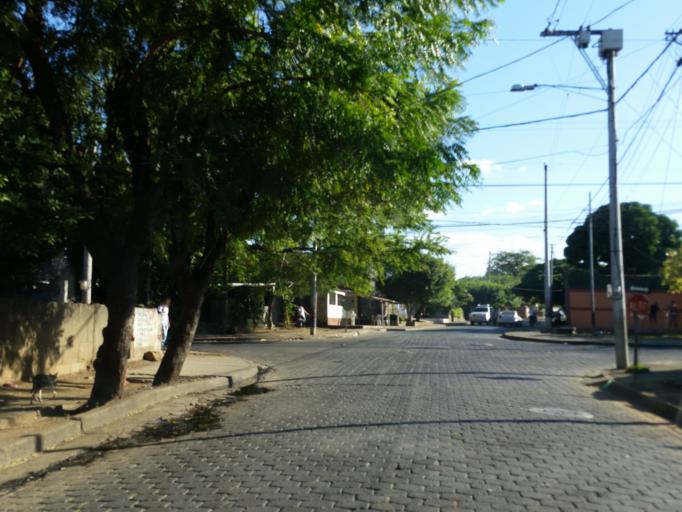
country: NI
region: Managua
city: Managua
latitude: 12.1312
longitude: -86.2918
